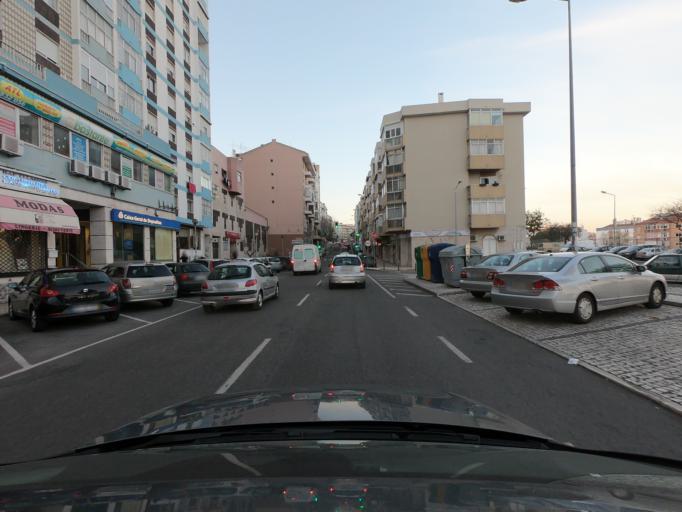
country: PT
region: Lisbon
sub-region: Sintra
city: Queluz
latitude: 38.7567
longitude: -9.2653
